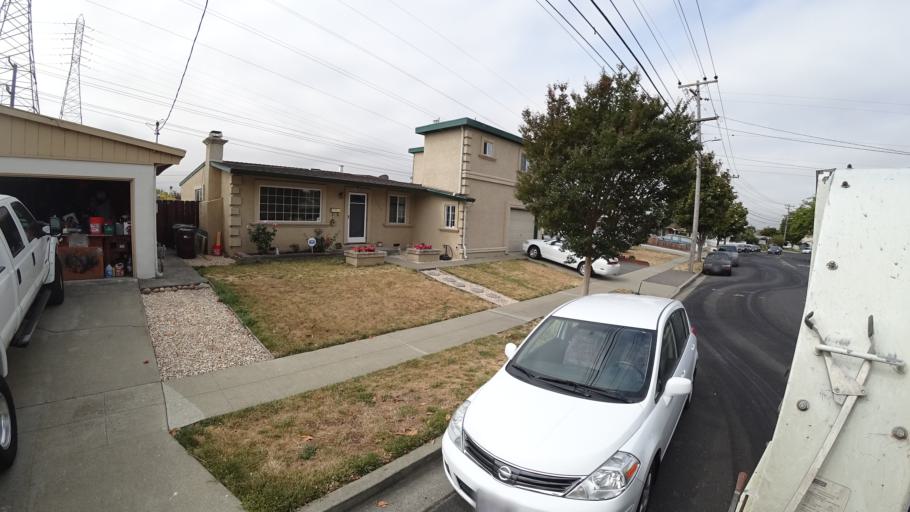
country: US
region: California
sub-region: Alameda County
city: Hayward
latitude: 37.6317
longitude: -122.1054
